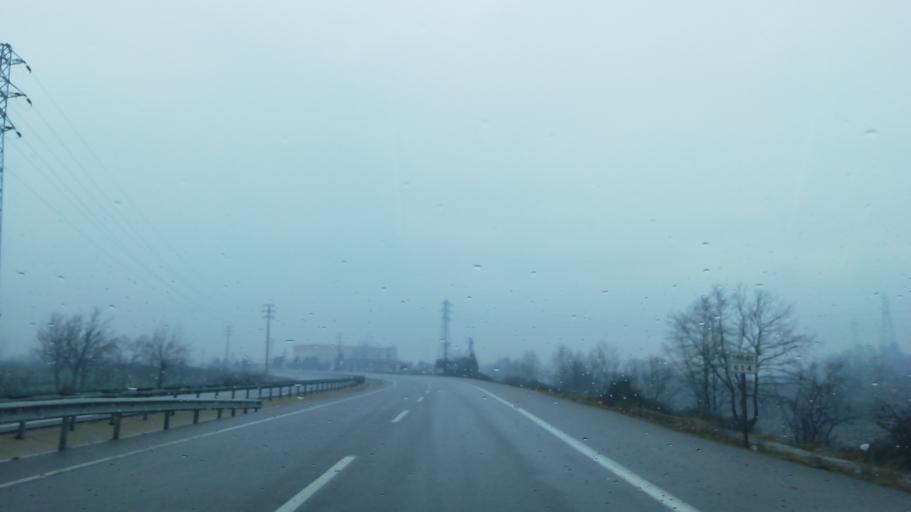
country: TR
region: Sakarya
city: Akyazi
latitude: 40.6429
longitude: 30.6130
